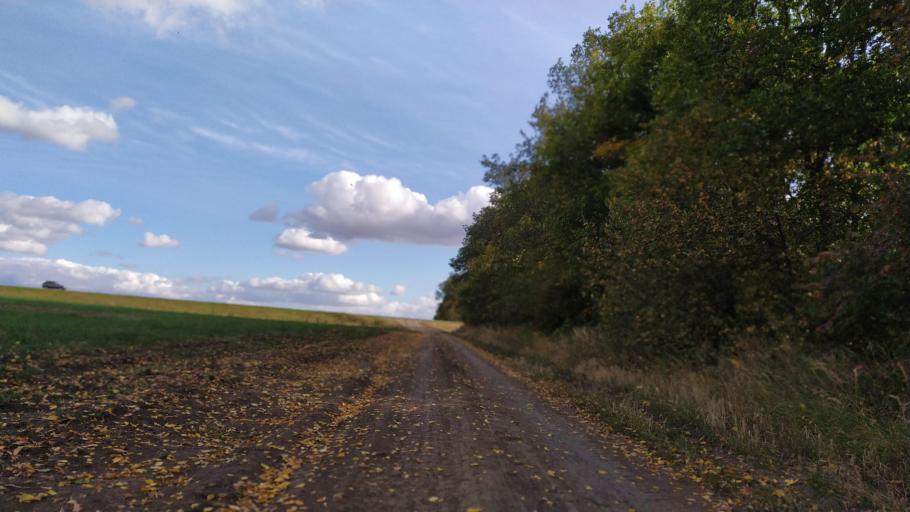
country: RU
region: Kursk
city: Kursk
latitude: 51.6163
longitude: 36.1643
